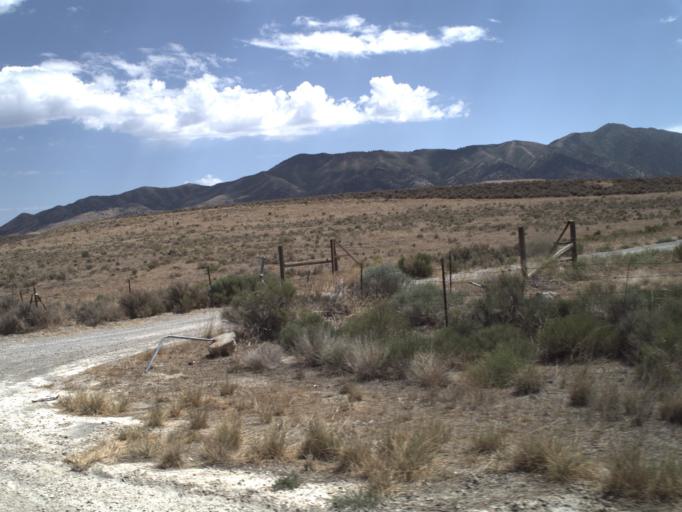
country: US
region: Utah
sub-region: Tooele County
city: Tooele
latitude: 40.4118
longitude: -112.3841
